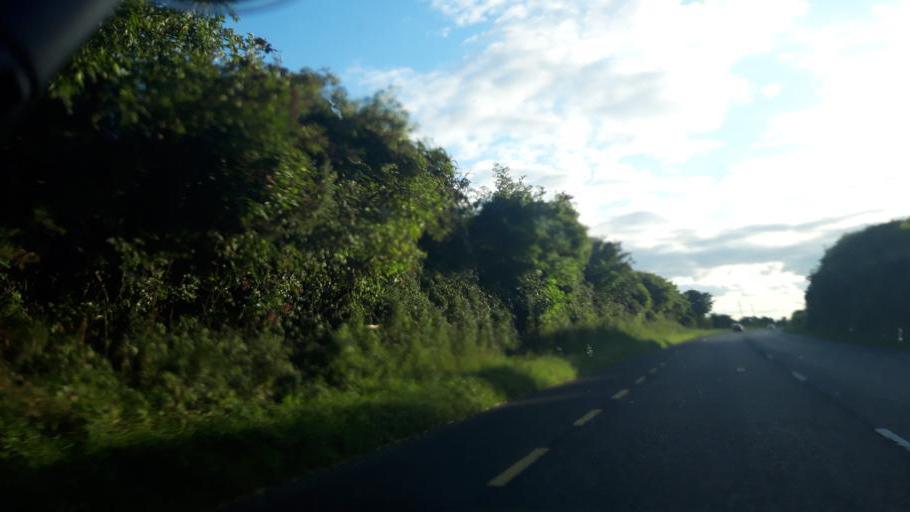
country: IE
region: Leinster
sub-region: Lu
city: Carlingford
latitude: 54.0024
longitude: -6.1821
